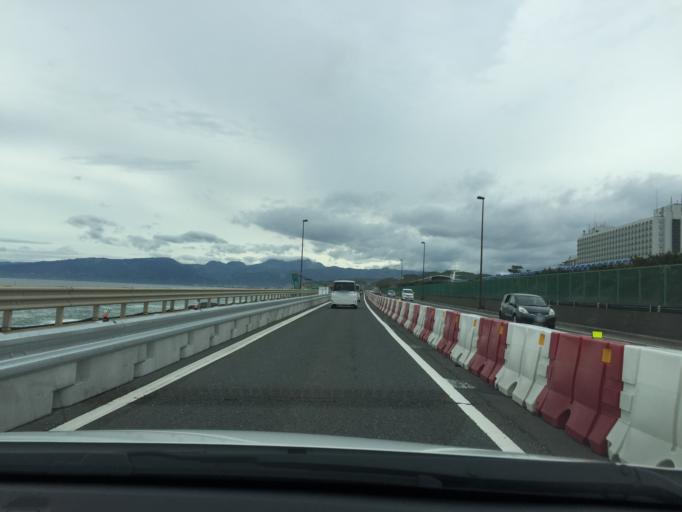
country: JP
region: Kanagawa
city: Oiso
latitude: 35.3006
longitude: 139.2844
